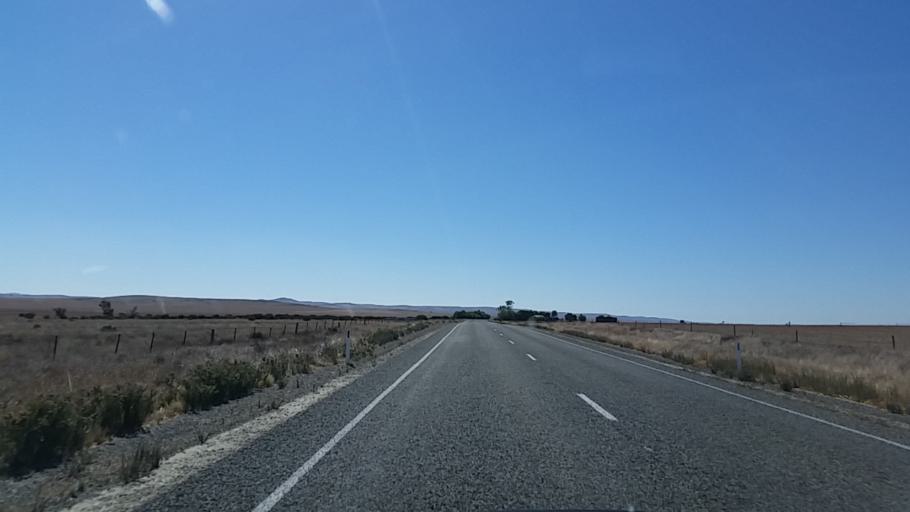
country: AU
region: South Australia
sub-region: Northern Areas
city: Jamestown
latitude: -33.2871
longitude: 138.8703
